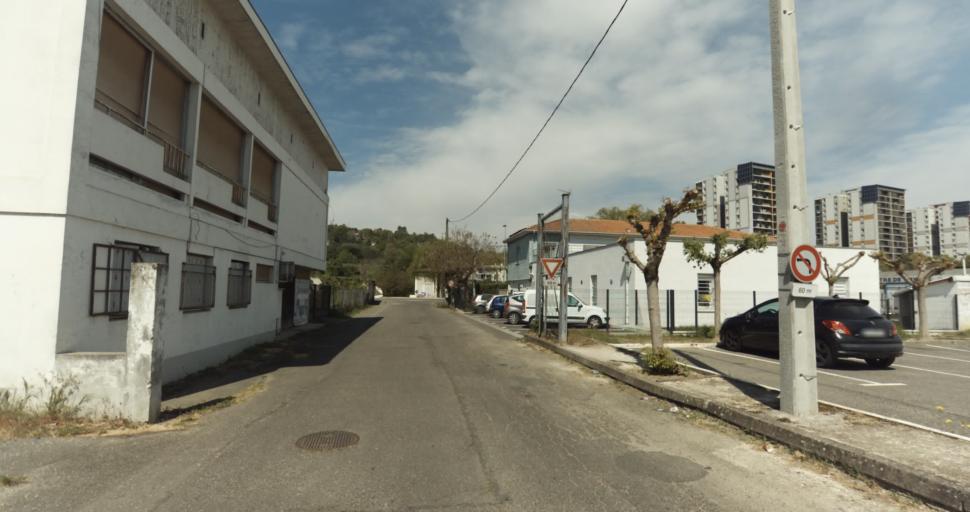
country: FR
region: Aquitaine
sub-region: Departement du Lot-et-Garonne
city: Agen
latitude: 44.2106
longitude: 0.6467
